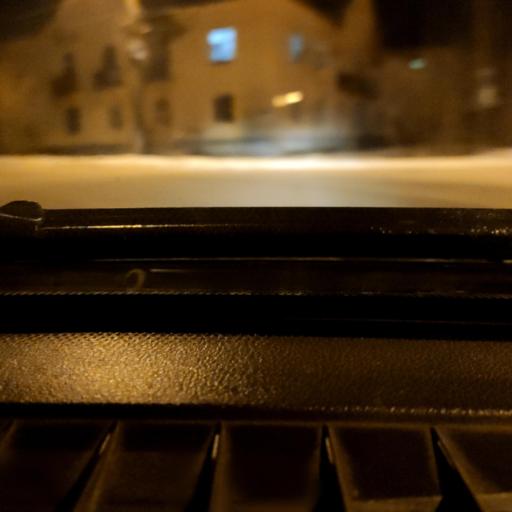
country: RU
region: Perm
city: Perm
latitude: 58.0881
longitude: 56.3855
